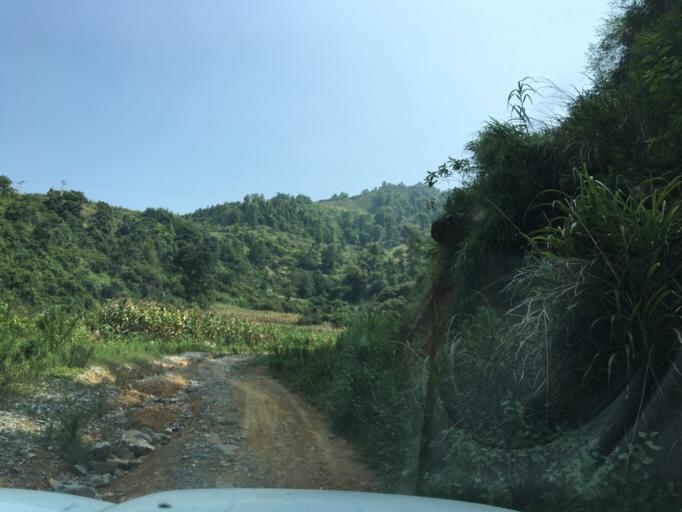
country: CN
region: Guangxi Zhuangzu Zizhiqu
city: Xinzhou
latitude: 24.9935
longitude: 105.7432
